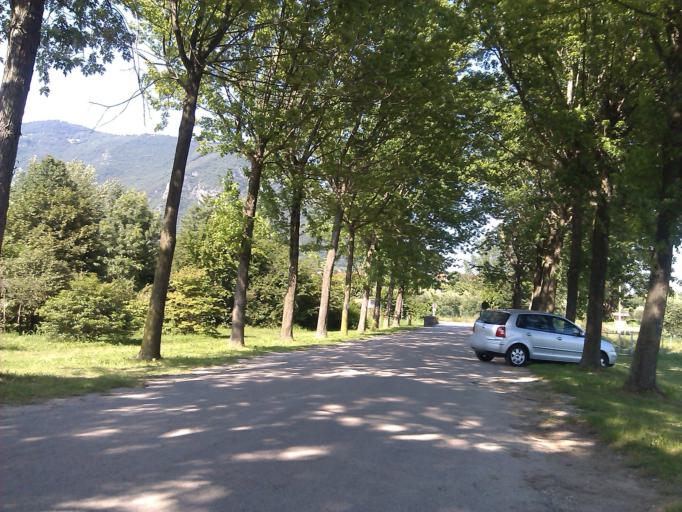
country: IT
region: Veneto
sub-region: Provincia di Vicenza
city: Pove del Grappa
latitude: 45.7864
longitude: 11.7286
